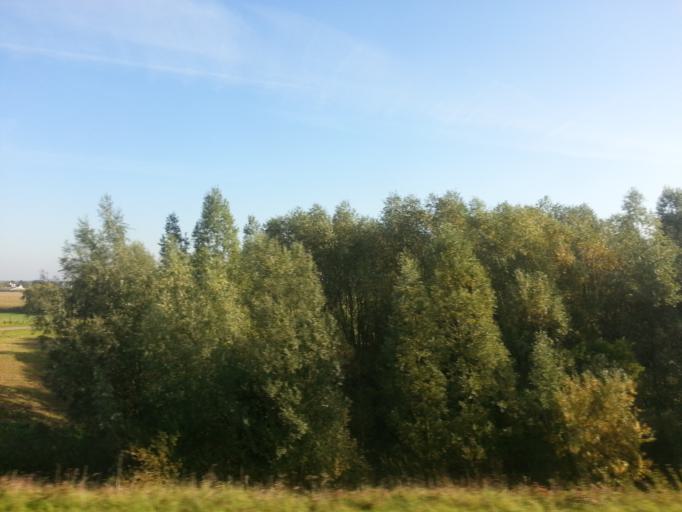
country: NL
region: Gelderland
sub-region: Gemeente Culemborg
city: Culemborg
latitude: 51.9664
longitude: 5.2080
